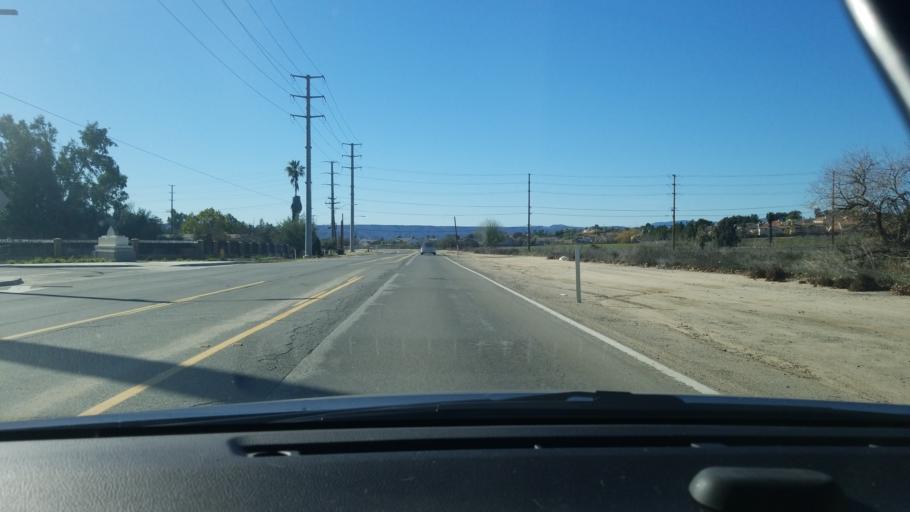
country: US
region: California
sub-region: Riverside County
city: Murrieta Hot Springs
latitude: 33.5431
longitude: -117.1167
